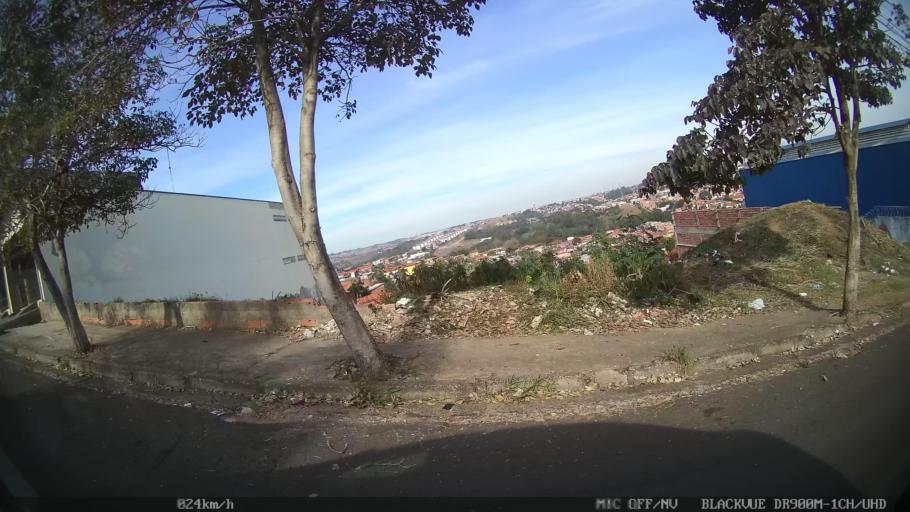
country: BR
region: Sao Paulo
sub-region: Piracicaba
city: Piracicaba
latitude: -22.7435
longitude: -47.6654
